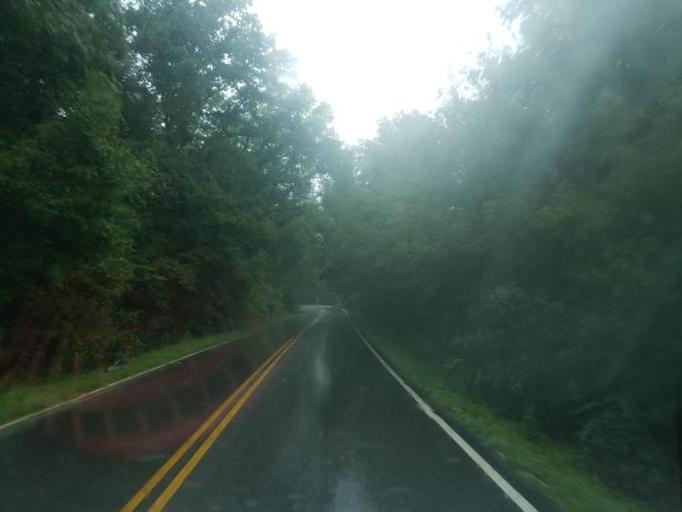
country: US
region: Kentucky
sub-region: Carter County
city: Grayson
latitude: 38.4922
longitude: -82.9912
